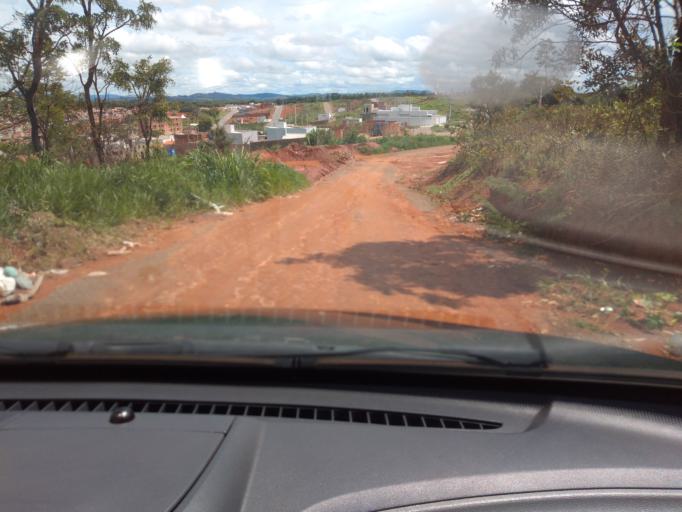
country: BR
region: Minas Gerais
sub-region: Tres Coracoes
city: Tres Coracoes
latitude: -21.6759
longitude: -45.2779
